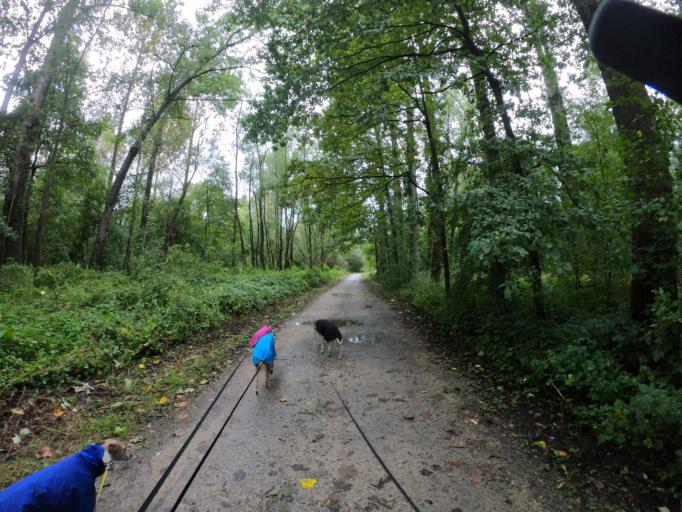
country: BE
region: Flanders
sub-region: Provincie Vlaams-Brabant
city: Rotselaar
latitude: 50.9501
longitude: 4.7330
